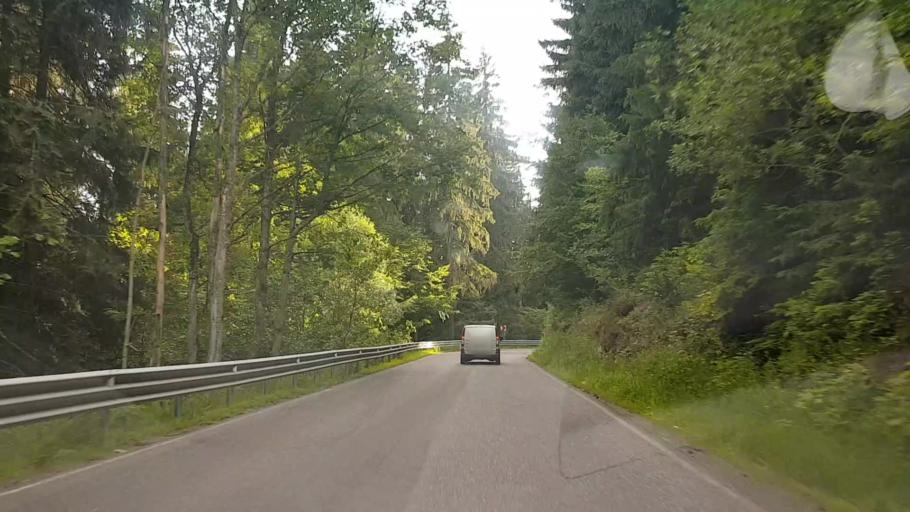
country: RO
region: Harghita
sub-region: Comuna Remetea
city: Remetea
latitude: 46.6718
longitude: 25.3529
